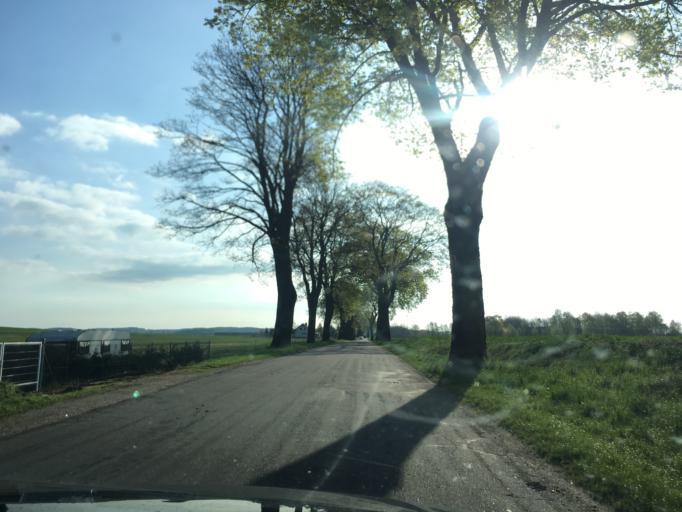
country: PL
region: Warmian-Masurian Voivodeship
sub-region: Powiat nidzicki
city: Kozlowo
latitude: 53.4048
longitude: 20.2871
